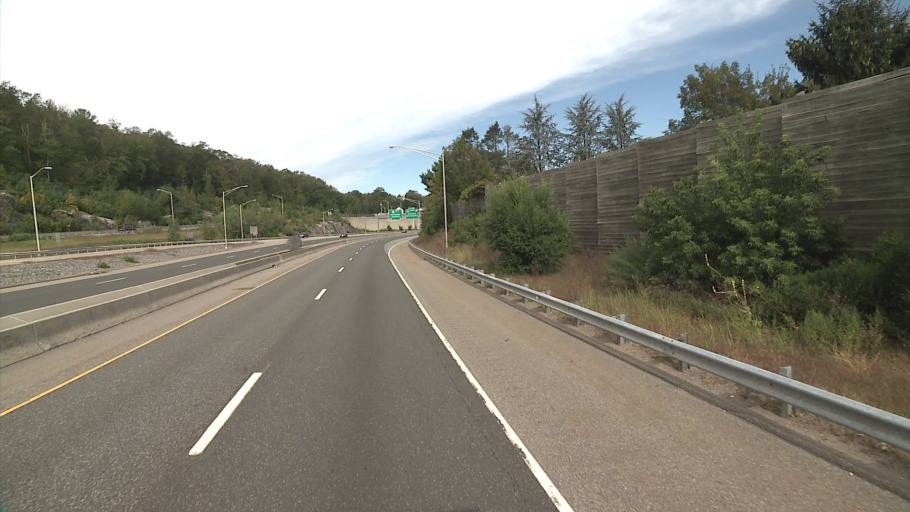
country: US
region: Connecticut
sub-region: New London County
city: Norwich
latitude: 41.5585
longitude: -72.1227
